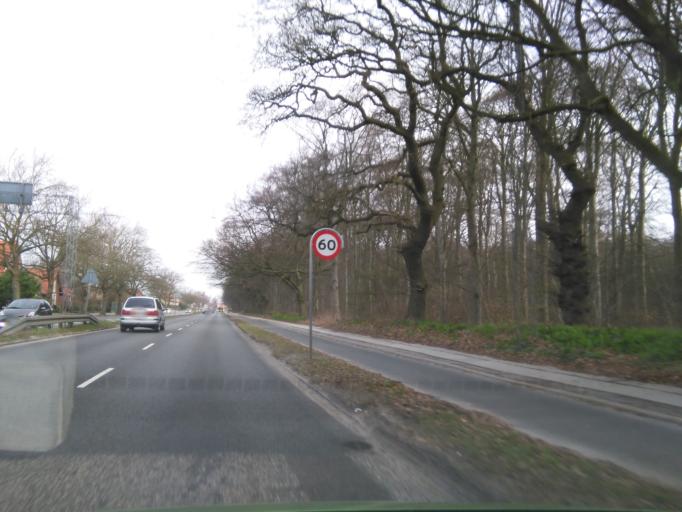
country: DK
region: Central Jutland
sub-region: Arhus Kommune
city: Arhus
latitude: 56.1785
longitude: 10.2186
